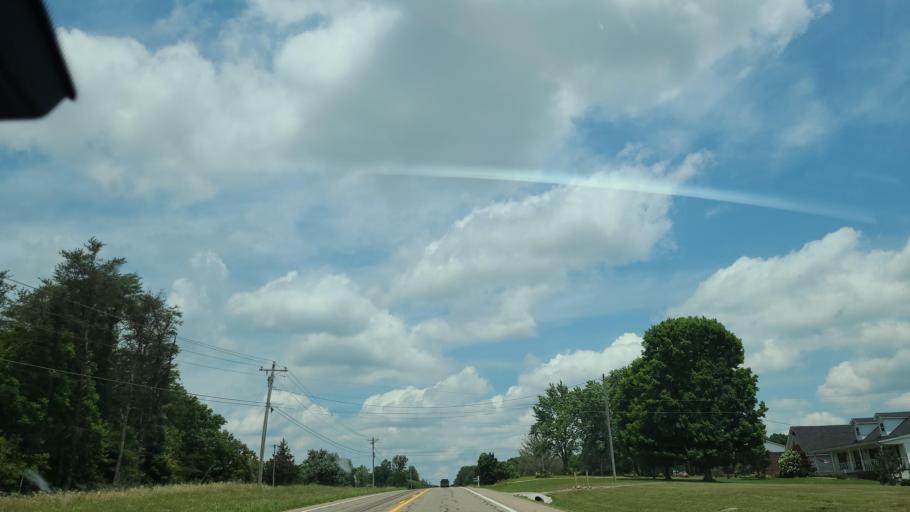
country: US
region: Tennessee
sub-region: Cumberland County
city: Lake Tansi
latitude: 35.8533
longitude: -85.0118
